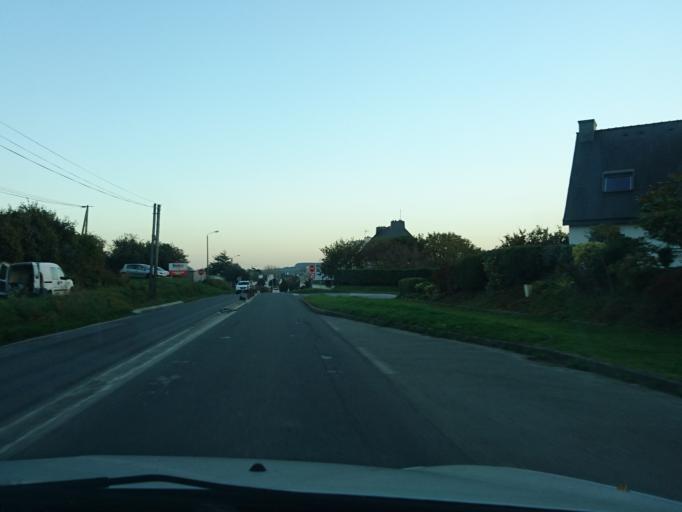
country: FR
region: Brittany
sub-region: Departement du Finistere
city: Saint-Renan
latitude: 48.4404
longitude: -4.6207
